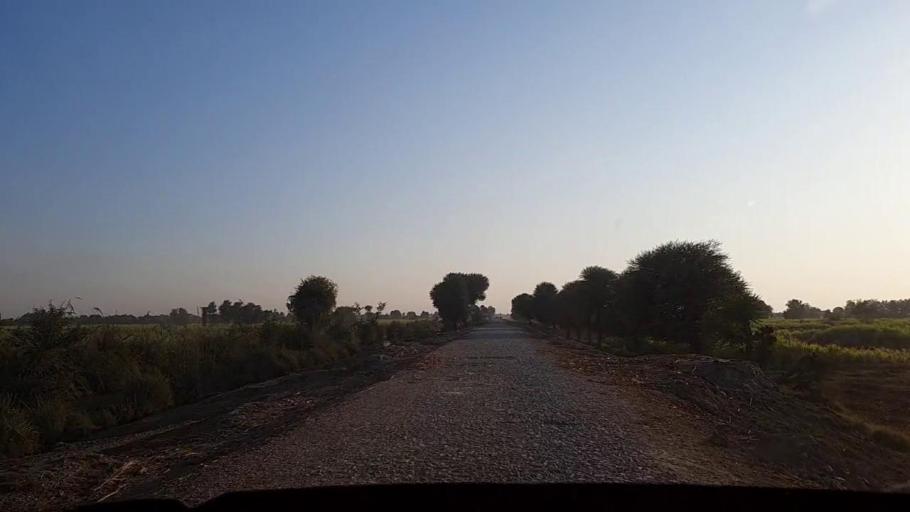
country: PK
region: Sindh
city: Sobhadero
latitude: 27.3753
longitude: 68.3792
